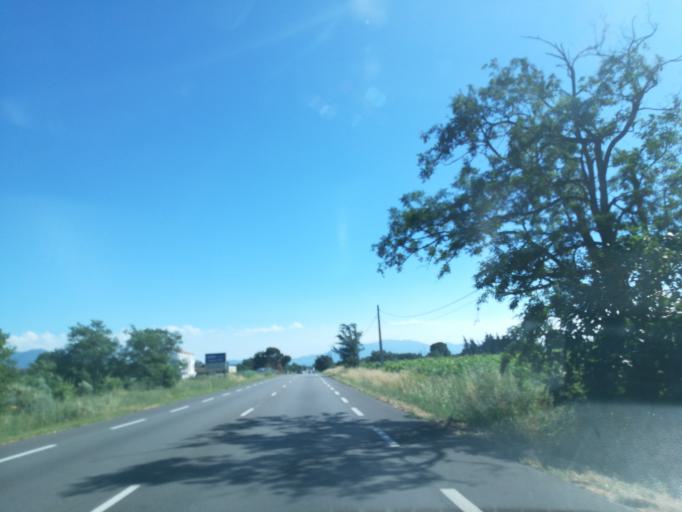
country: FR
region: Languedoc-Roussillon
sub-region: Departement des Pyrenees-Orientales
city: Pollestres
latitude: 42.6241
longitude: 2.8679
